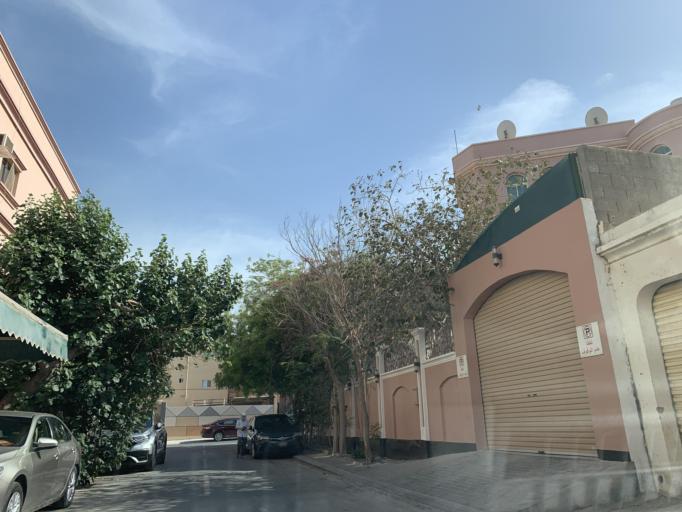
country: BH
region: Northern
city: Ar Rifa'
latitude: 26.1249
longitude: 50.5812
